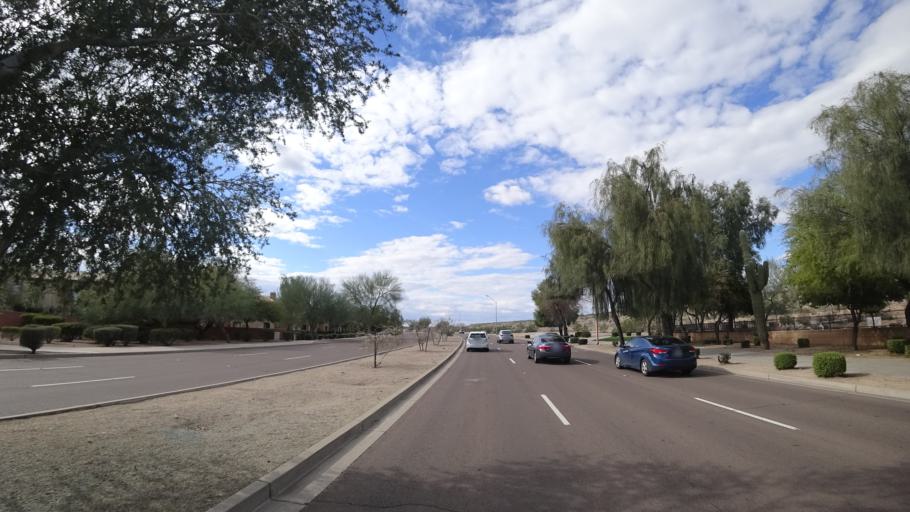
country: US
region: Arizona
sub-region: Maricopa County
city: Paradise Valley
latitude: 33.6288
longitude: -111.8821
